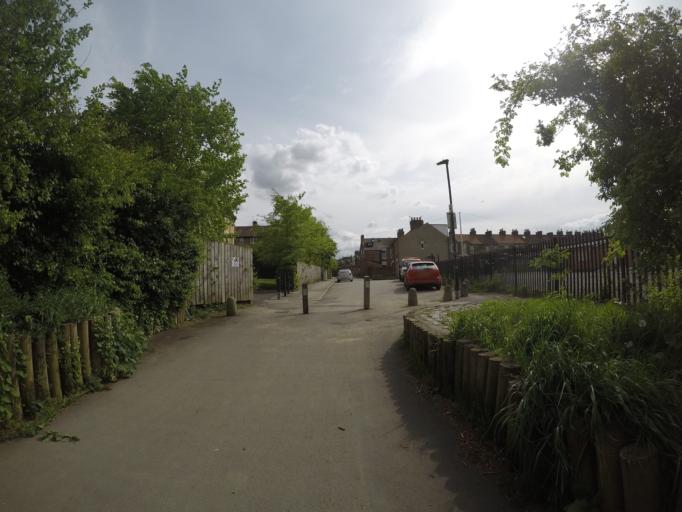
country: GB
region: England
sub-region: City of York
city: Heslington
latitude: 53.9564
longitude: -1.0629
